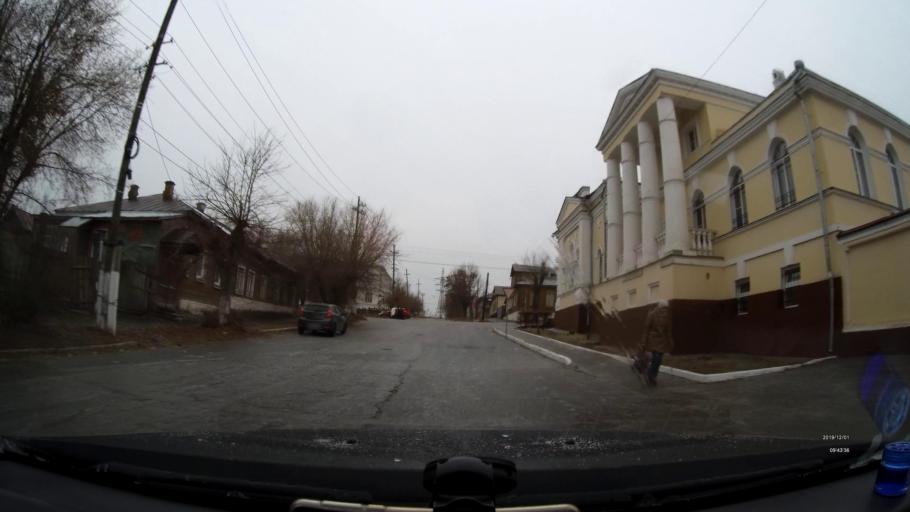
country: RU
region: Saratov
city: Vol'sk
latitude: 52.0430
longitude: 47.3819
